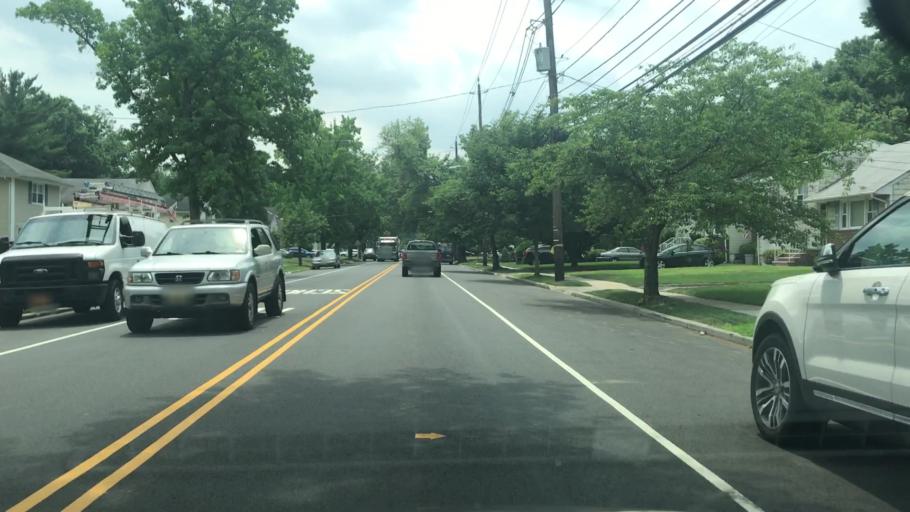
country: US
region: New Jersey
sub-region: Union County
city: Clark
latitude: 40.6446
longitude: -74.3049
